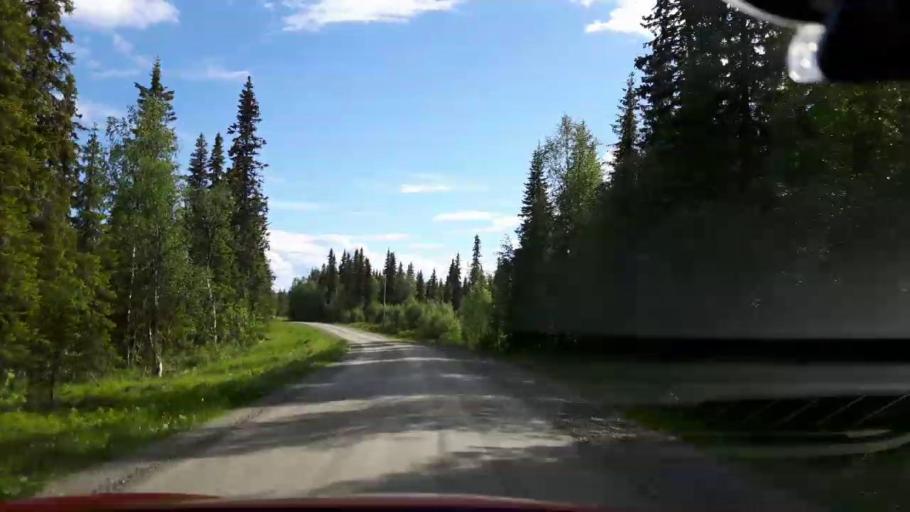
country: SE
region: Jaemtland
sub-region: Krokoms Kommun
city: Valla
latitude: 63.8063
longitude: 14.0495
